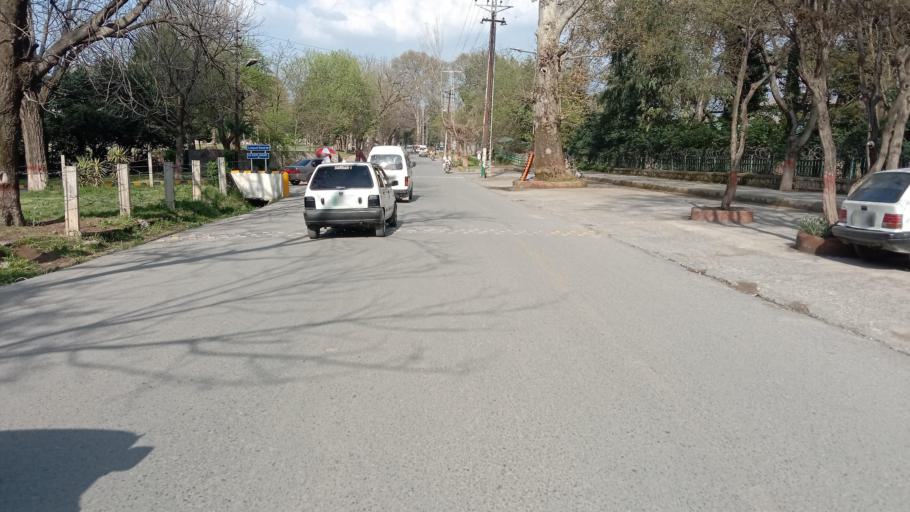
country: PK
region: Khyber Pakhtunkhwa
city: Abbottabad
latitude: 34.1508
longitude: 73.2154
